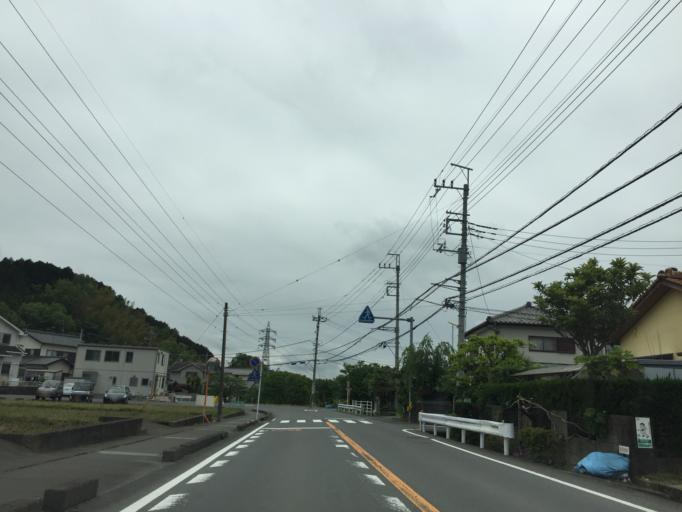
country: JP
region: Shizuoka
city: Gotemba
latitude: 35.2118
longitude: 138.9245
